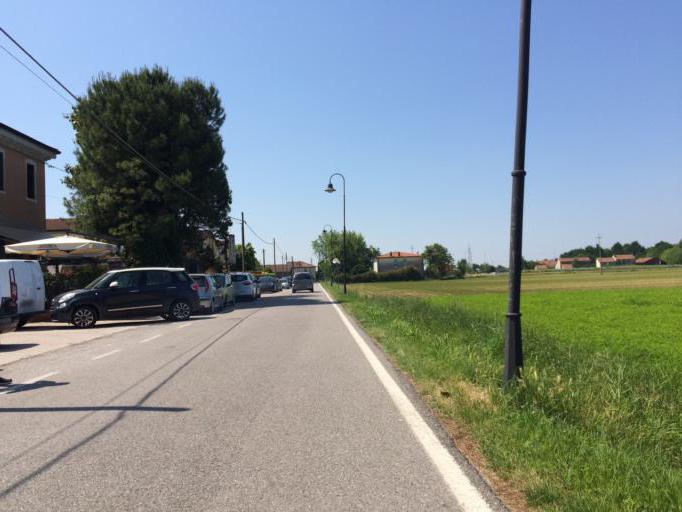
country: IT
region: Veneto
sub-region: Provincia di Vicenza
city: Villaganzerla
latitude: 45.4487
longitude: 11.6391
